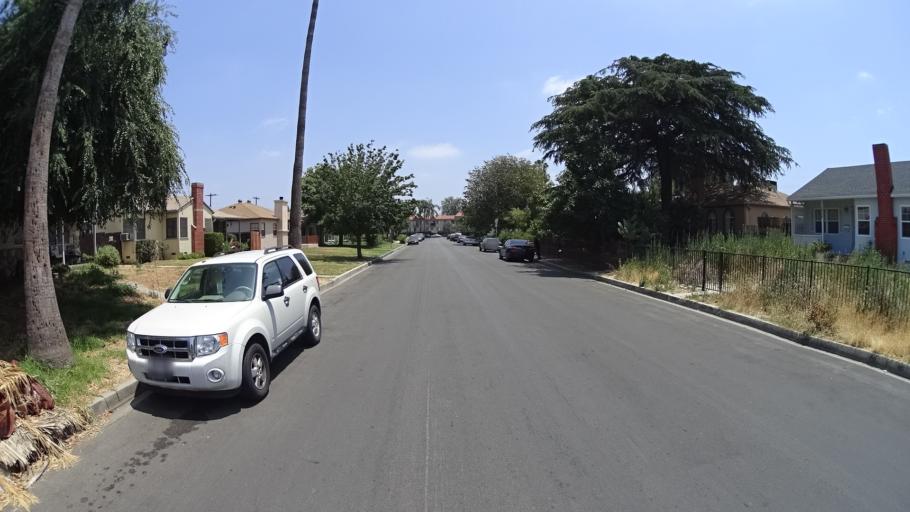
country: US
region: California
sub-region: Los Angeles County
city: Van Nuys
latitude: 34.1962
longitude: -118.4592
